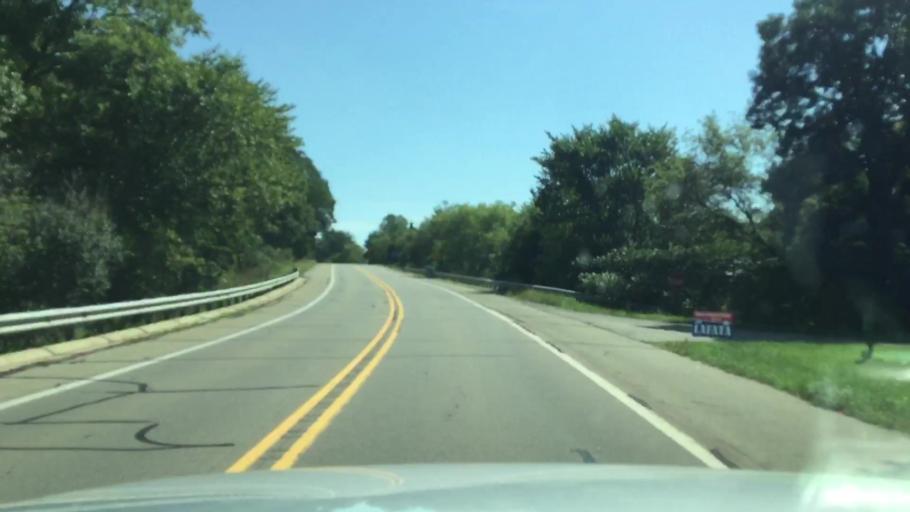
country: US
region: Michigan
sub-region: Jackson County
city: Brooklyn
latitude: 42.0581
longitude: -84.1758
